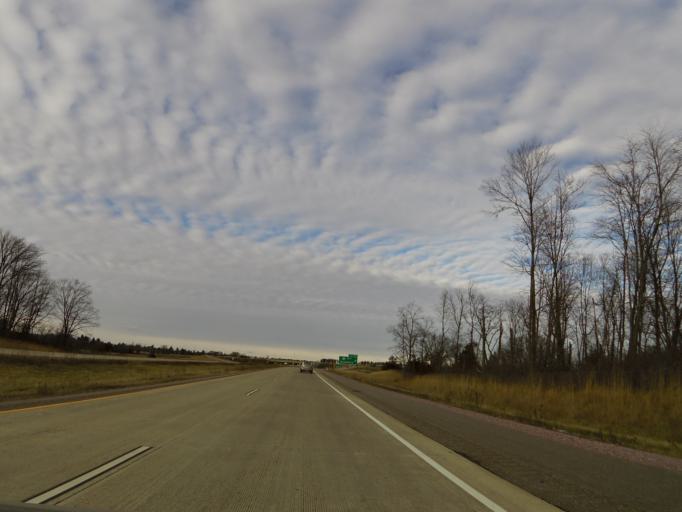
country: US
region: Wisconsin
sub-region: Sauk County
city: West Baraboo
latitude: 43.5089
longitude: -89.7818
